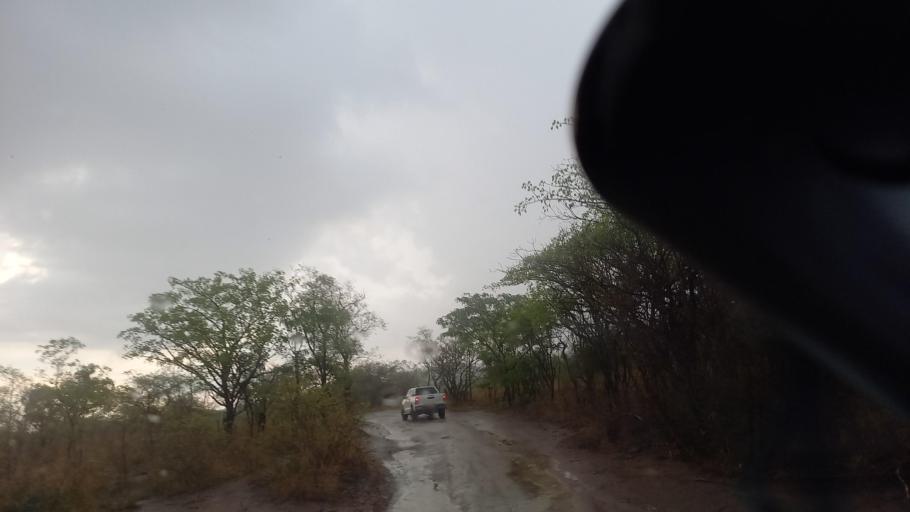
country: ZM
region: Lusaka
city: Kafue
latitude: -15.9439
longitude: 28.2177
